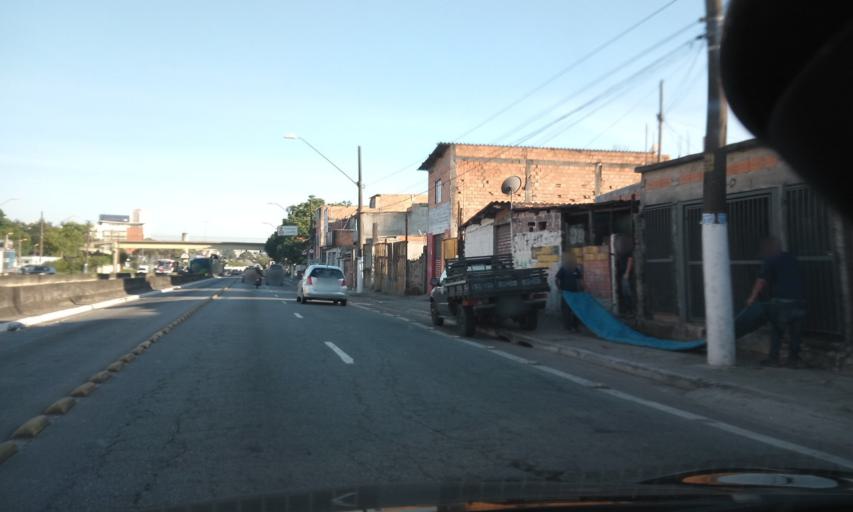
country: BR
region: Sao Paulo
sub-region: Santo Andre
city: Santo Andre
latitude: -23.6943
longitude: -46.5065
